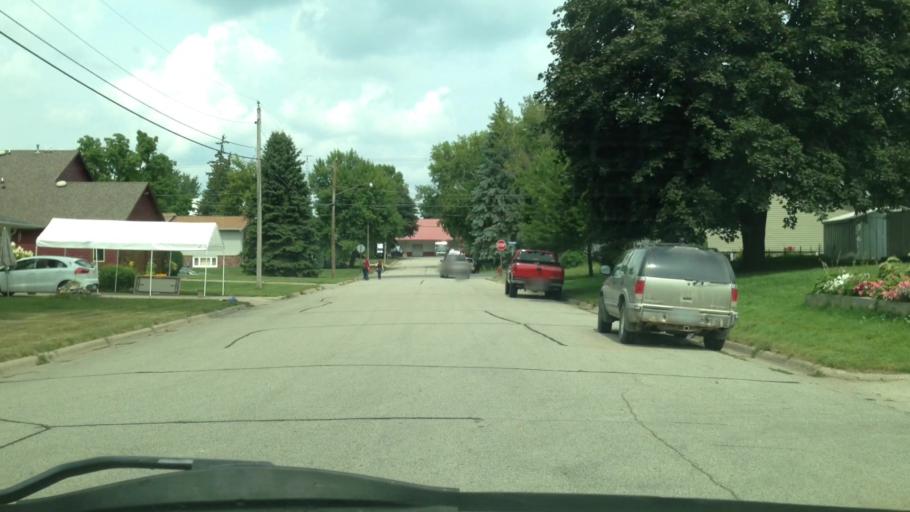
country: US
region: Minnesota
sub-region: Wabasha County
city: Plainview
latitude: 44.1621
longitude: -92.1740
